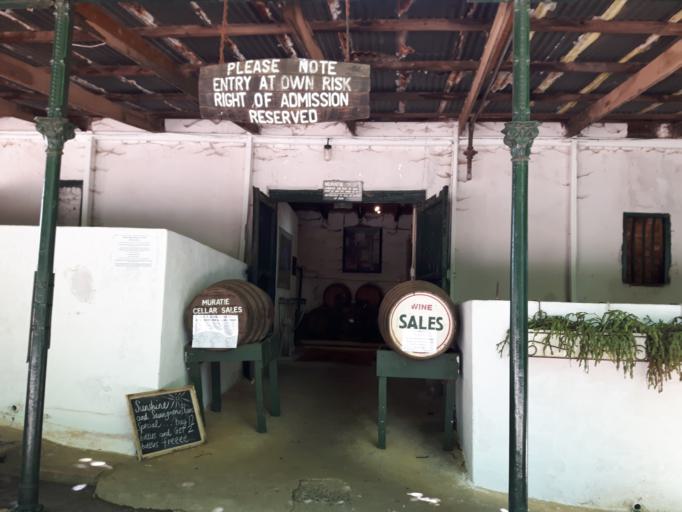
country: ZA
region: Western Cape
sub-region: Cape Winelands District Municipality
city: Stellenbosch
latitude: -33.8706
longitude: 18.8763
